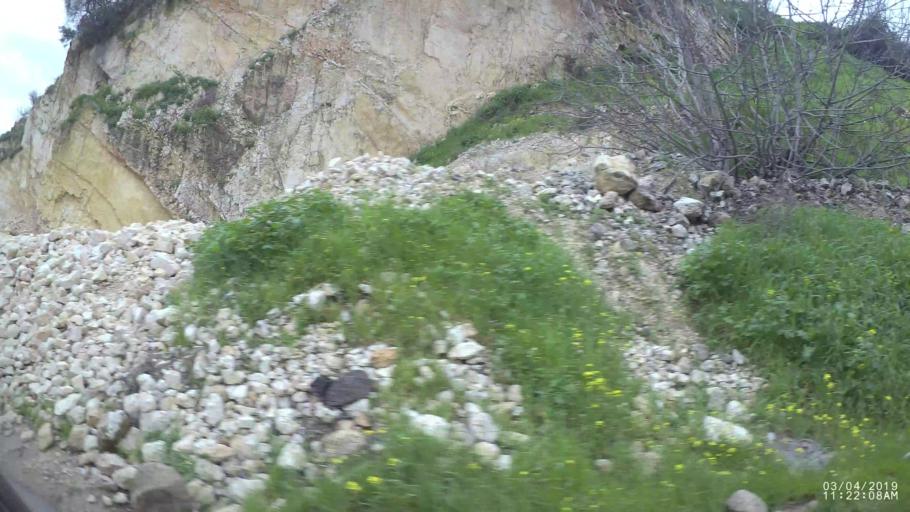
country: JO
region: Amman
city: Wadi as Sir
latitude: 31.9599
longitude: 35.8125
